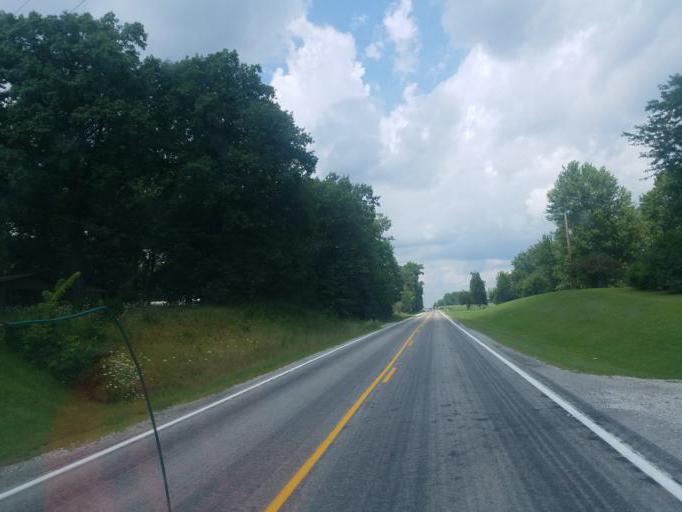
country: US
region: Ohio
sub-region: Crawford County
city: Bucyrus
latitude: 40.7511
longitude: -82.9071
